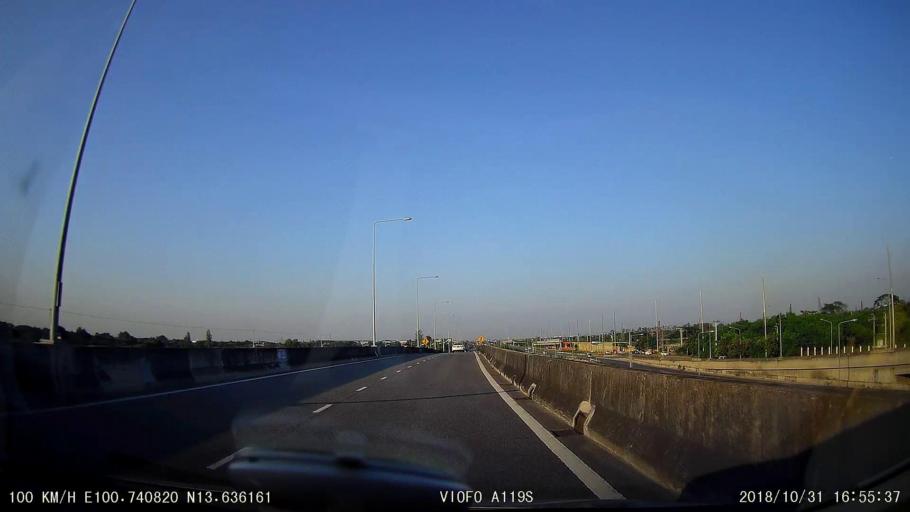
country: TH
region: Samut Prakan
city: Ban Khlong Bang Sao Thong
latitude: 13.6364
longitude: 100.7408
